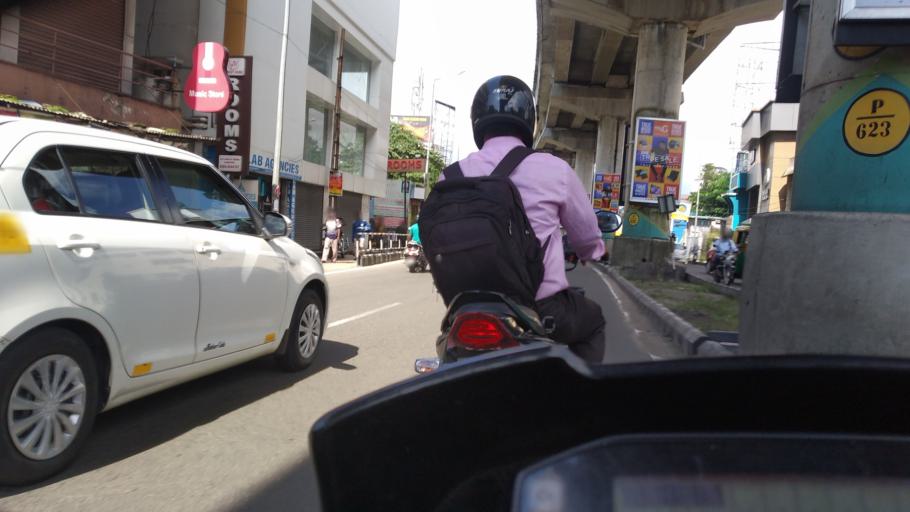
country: IN
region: Kerala
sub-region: Ernakulam
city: Cochin
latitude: 9.9869
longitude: 76.2845
